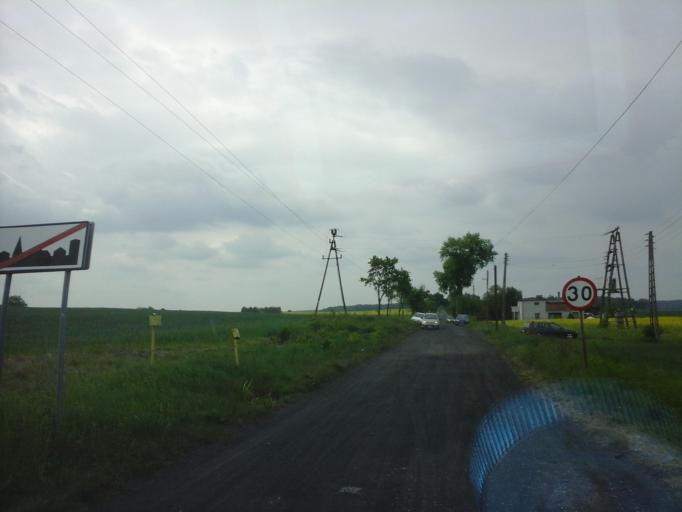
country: PL
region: West Pomeranian Voivodeship
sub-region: Powiat choszczenski
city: Pelczyce
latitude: 53.0171
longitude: 15.3705
